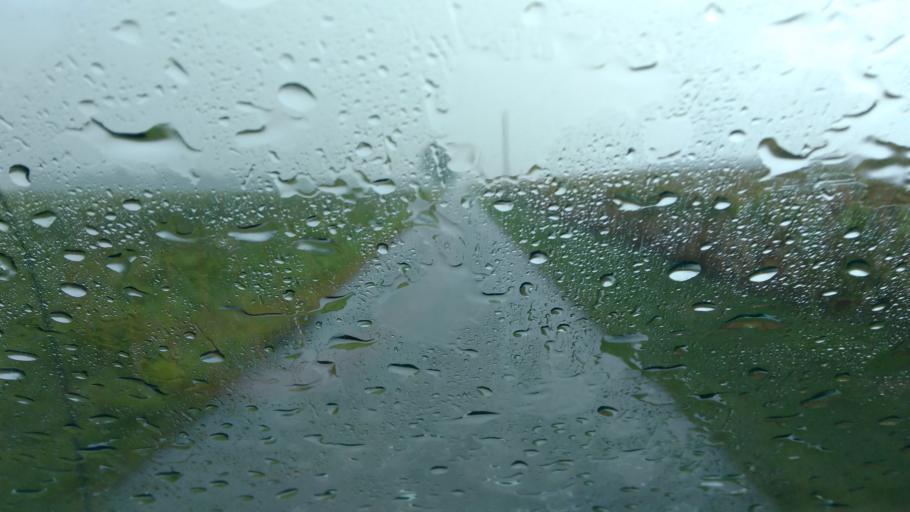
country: US
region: Ohio
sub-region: Hardin County
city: Forest
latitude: 40.7164
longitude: -83.5474
